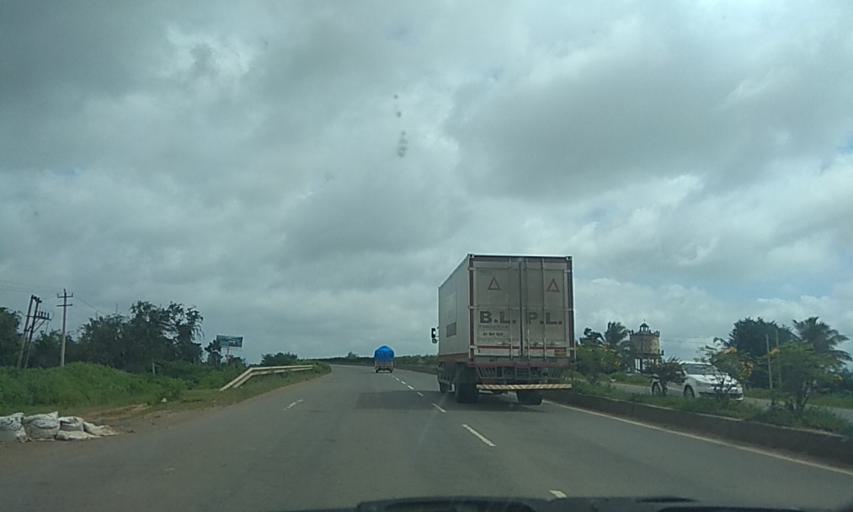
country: IN
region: Karnataka
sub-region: Dharwad
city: Hubli
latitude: 15.2468
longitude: 75.1448
